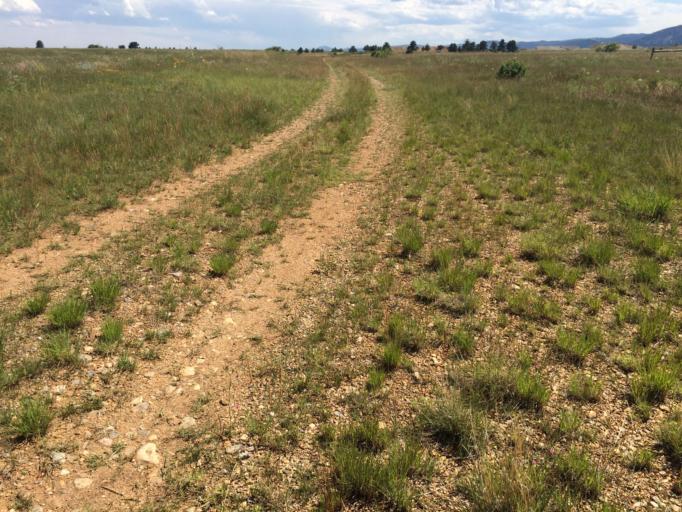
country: US
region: Colorado
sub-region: Boulder County
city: Superior
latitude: 39.9002
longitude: -105.2220
